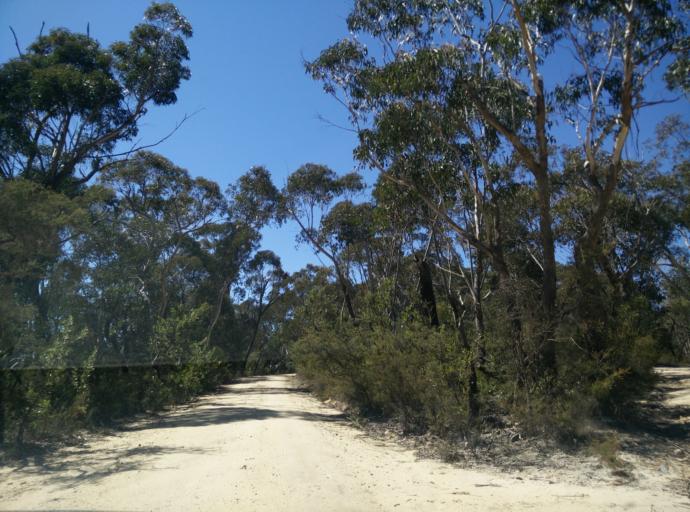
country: AU
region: New South Wales
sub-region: Blue Mountains Municipality
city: Blackheath
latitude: -33.5736
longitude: 150.2914
